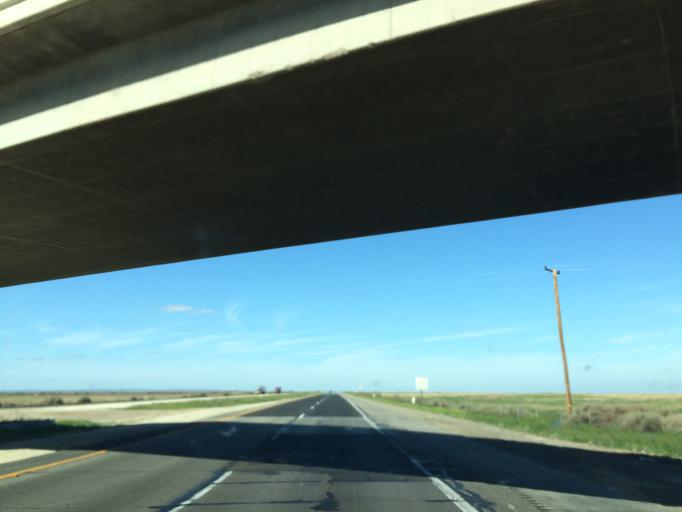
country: US
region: California
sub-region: Kern County
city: Lost Hills
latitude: 35.7894
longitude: -119.7820
